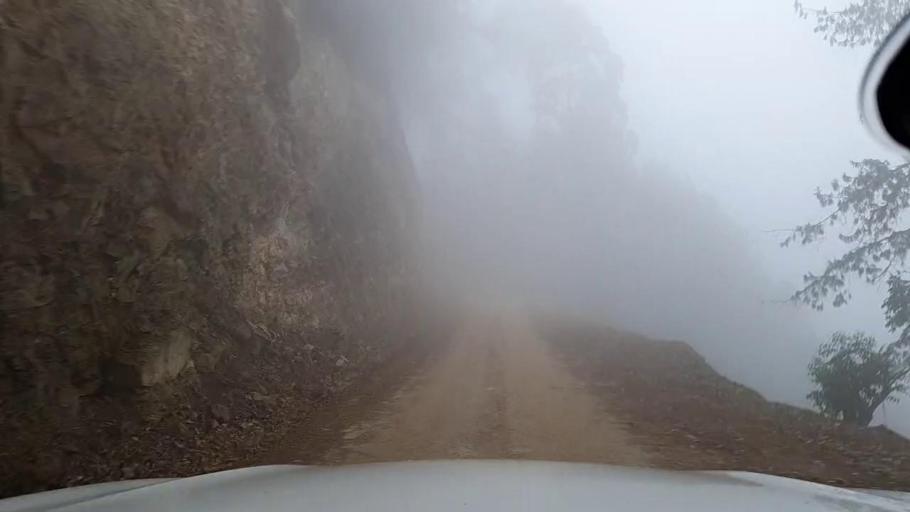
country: BI
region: Cibitoke
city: Cibitoke
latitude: -2.5937
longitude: 29.1924
